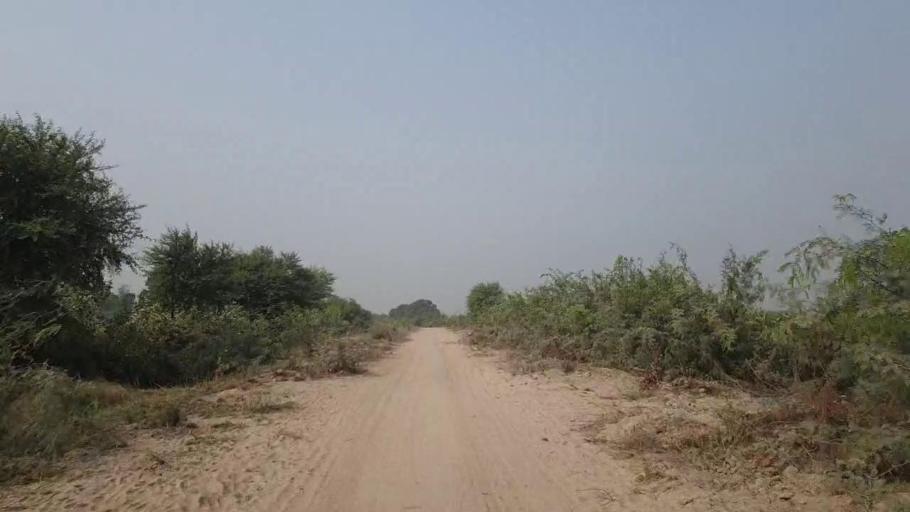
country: PK
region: Sindh
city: Tando Muhammad Khan
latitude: 25.1946
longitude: 68.5764
